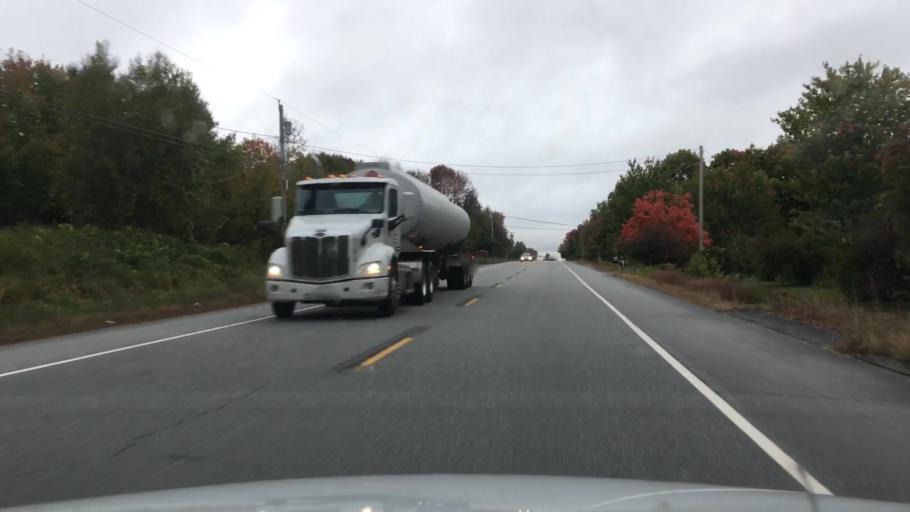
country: US
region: Maine
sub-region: Androscoggin County
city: Mechanic Falls
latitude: 44.1110
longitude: -70.4396
